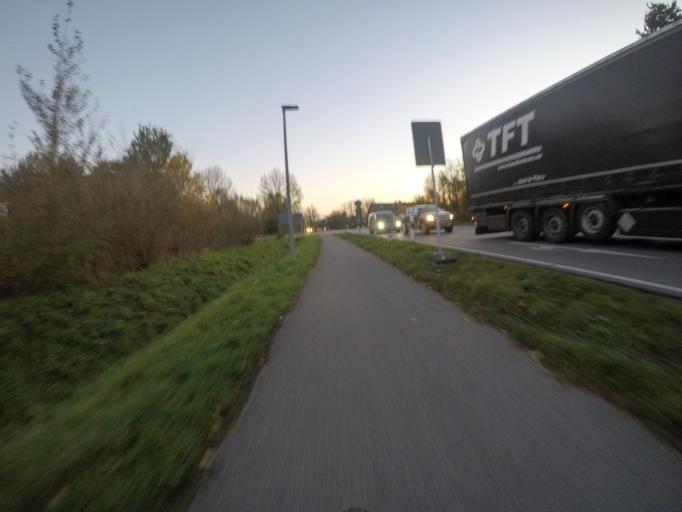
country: DE
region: North Rhine-Westphalia
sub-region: Regierungsbezirk Dusseldorf
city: Bocholt
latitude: 51.8113
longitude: 6.5695
